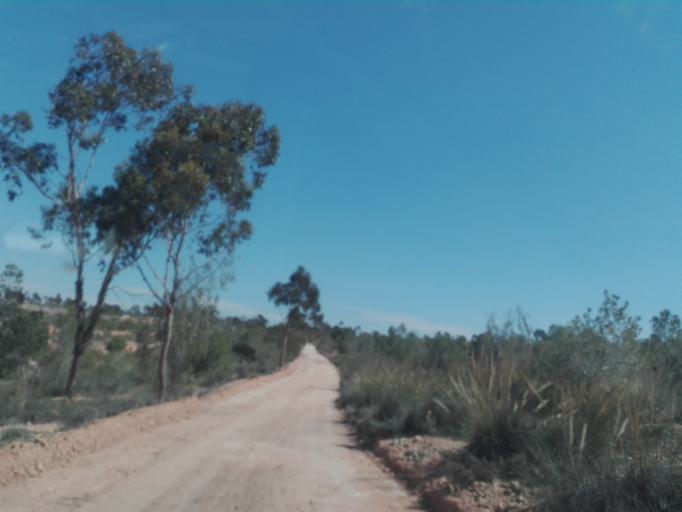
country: TN
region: Safaqis
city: Sfax
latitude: 34.6979
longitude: 10.5302
